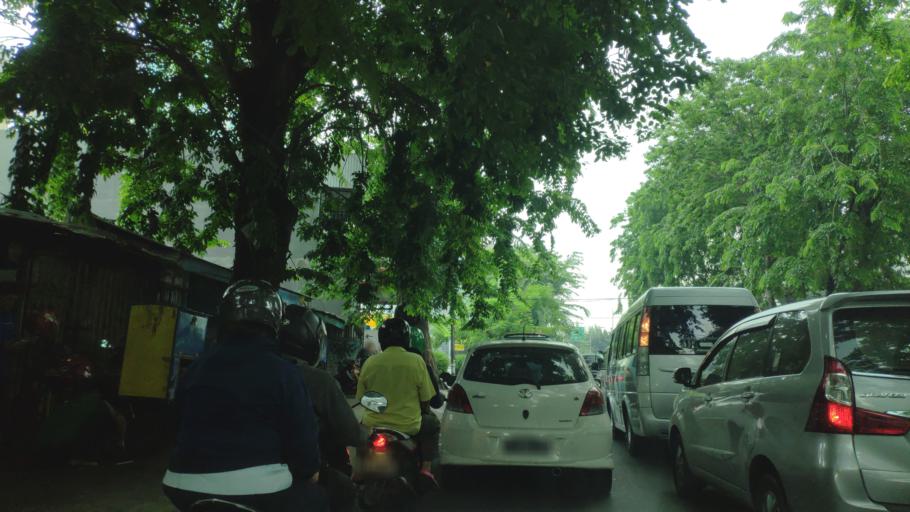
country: ID
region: Jakarta Raya
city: Jakarta
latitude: -6.2030
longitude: 106.7978
